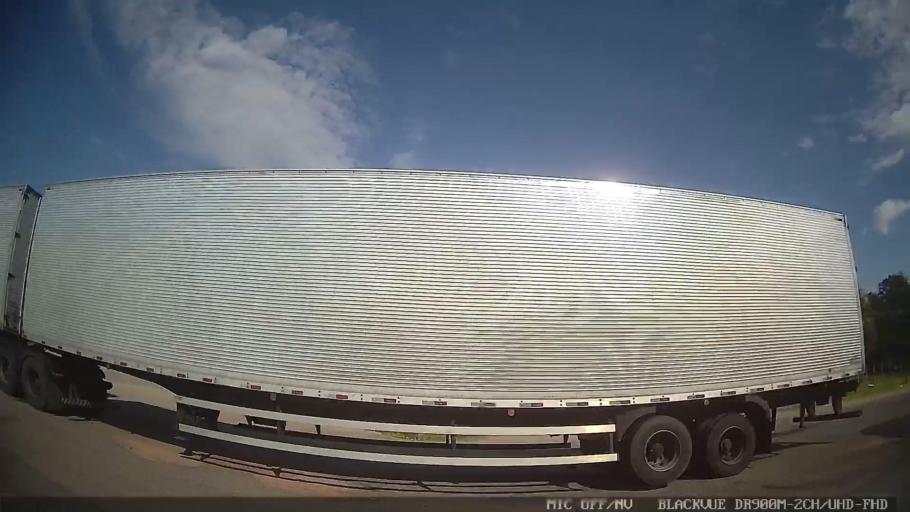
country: BR
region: Sao Paulo
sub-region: Jarinu
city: Jarinu
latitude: -23.0632
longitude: -46.6831
